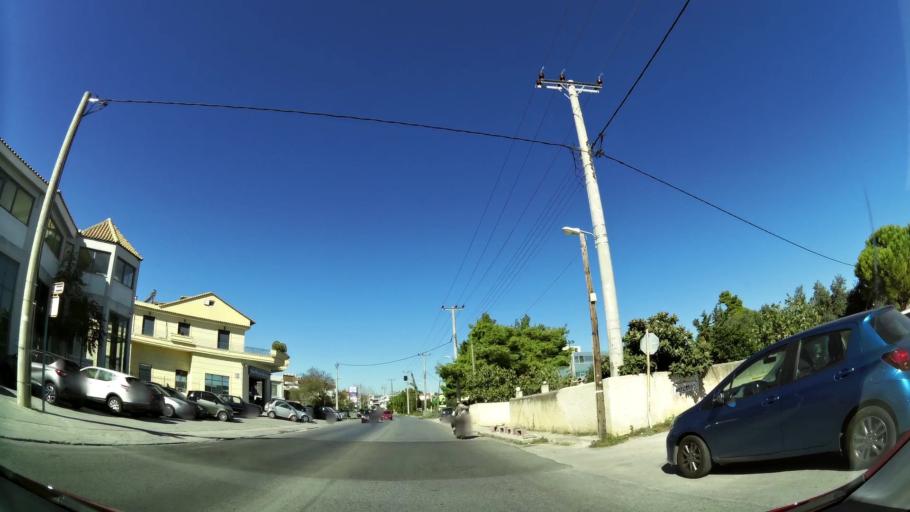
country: GR
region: Attica
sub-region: Nomarchia Anatolikis Attikis
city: Leondarion
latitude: 38.0012
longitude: 23.8600
